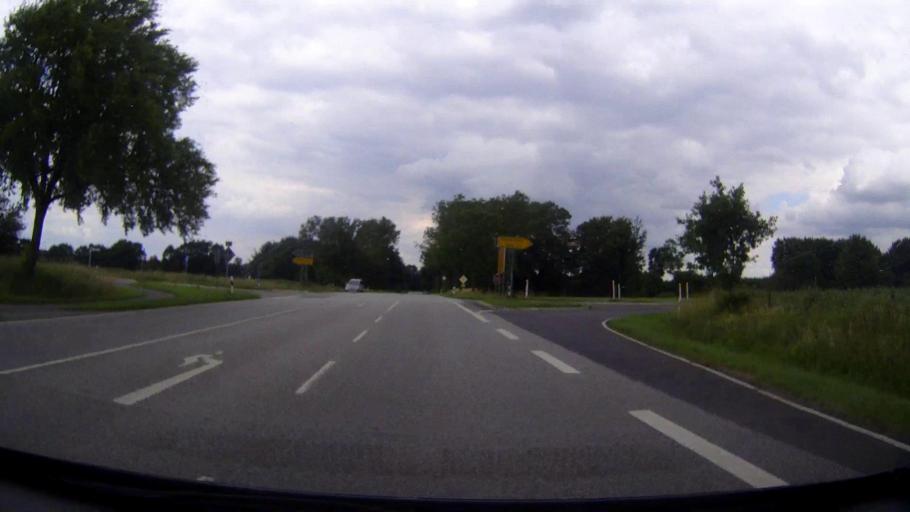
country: DE
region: Schleswig-Holstein
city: Reher
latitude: 54.0650
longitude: 9.5627
